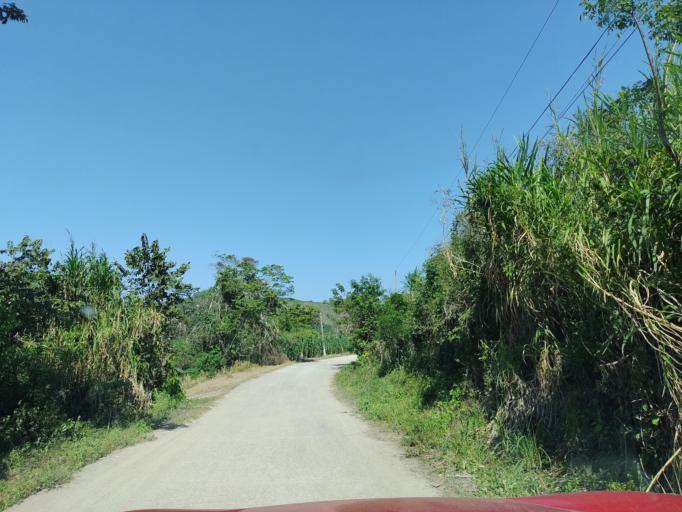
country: MX
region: Veracruz
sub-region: Papantla
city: Polutla
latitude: 20.4897
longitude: -97.1864
